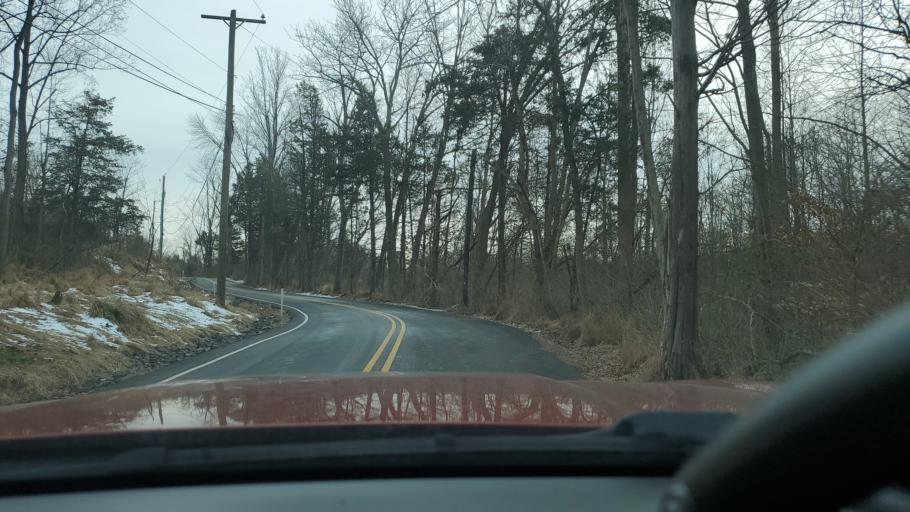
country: US
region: Pennsylvania
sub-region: Montgomery County
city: Red Hill
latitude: 40.3204
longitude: -75.5120
